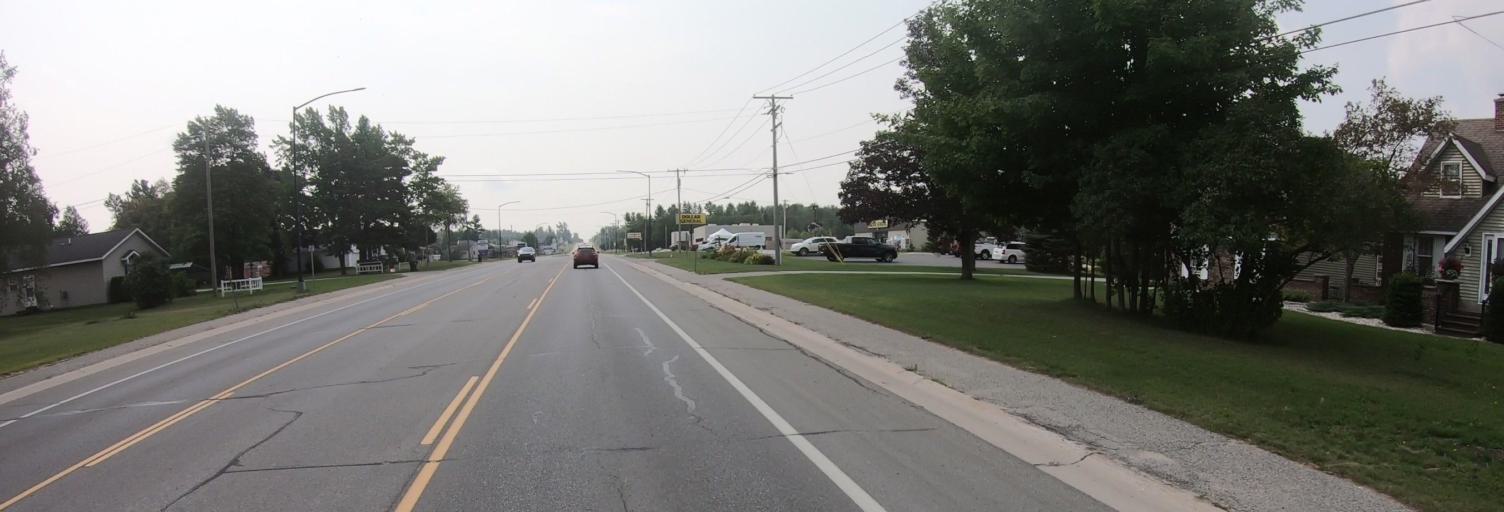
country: US
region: Michigan
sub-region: Luce County
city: Newberry
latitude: 46.3446
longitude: -85.5097
